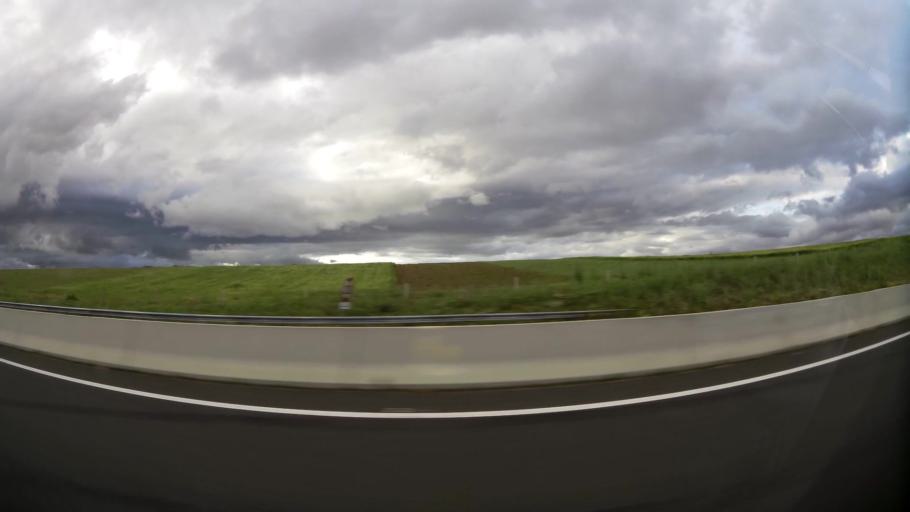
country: MA
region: Taza-Al Hoceima-Taounate
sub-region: Taza
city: Taza
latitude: 34.2518
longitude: -3.9207
